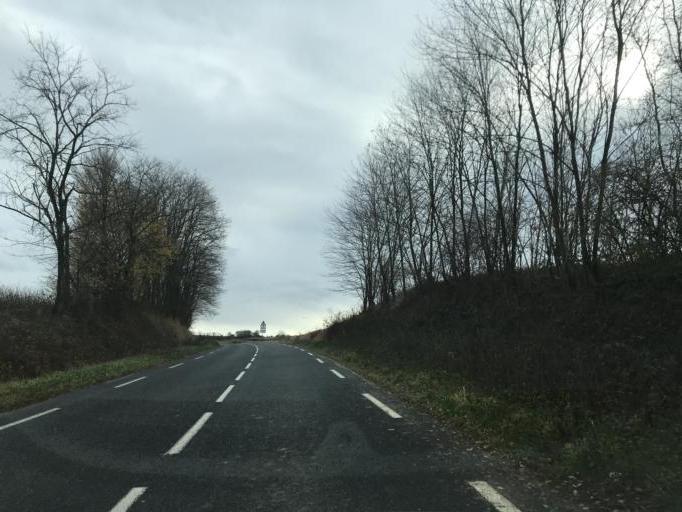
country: FR
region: Rhone-Alpes
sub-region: Departement de l'Ain
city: Miribel
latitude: 45.8457
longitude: 4.9362
